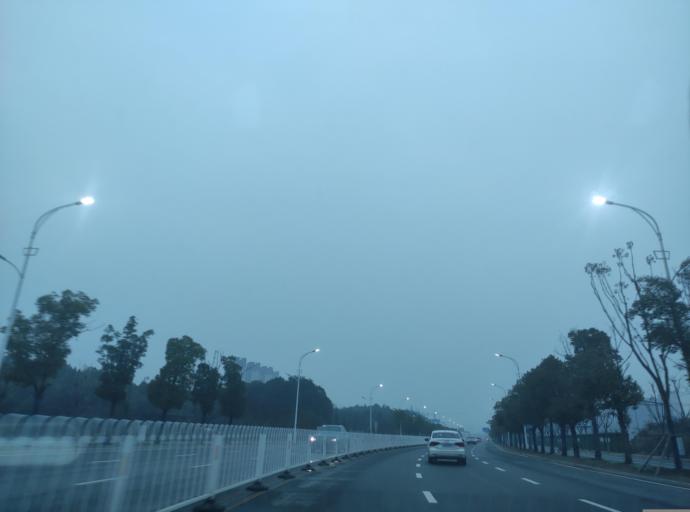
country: CN
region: Jiangxi Sheng
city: Pingxiang
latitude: 27.6691
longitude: 113.8571
